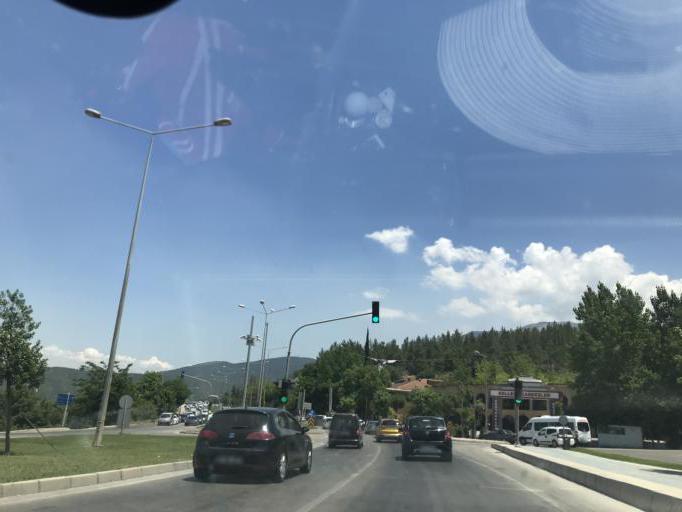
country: TR
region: Denizli
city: Denizli
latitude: 37.7306
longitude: 29.1547
